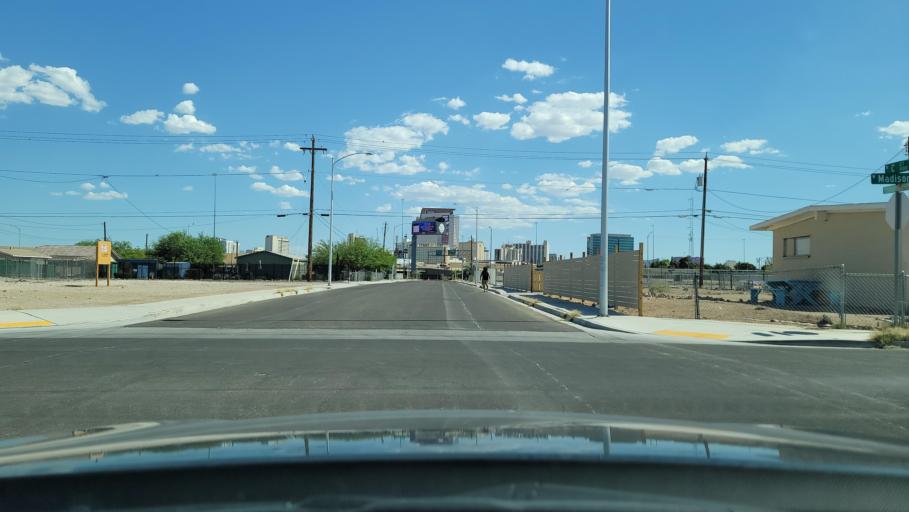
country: US
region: Nevada
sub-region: Clark County
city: Las Vegas
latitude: 36.1841
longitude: -115.1458
